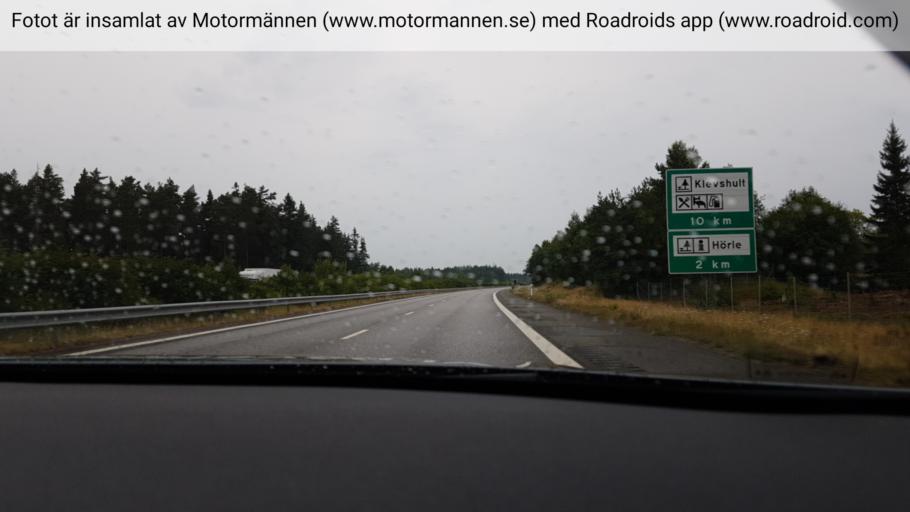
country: SE
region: Joenkoeping
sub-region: Varnamo Kommun
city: Varnamo
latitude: 57.2356
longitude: 14.0773
